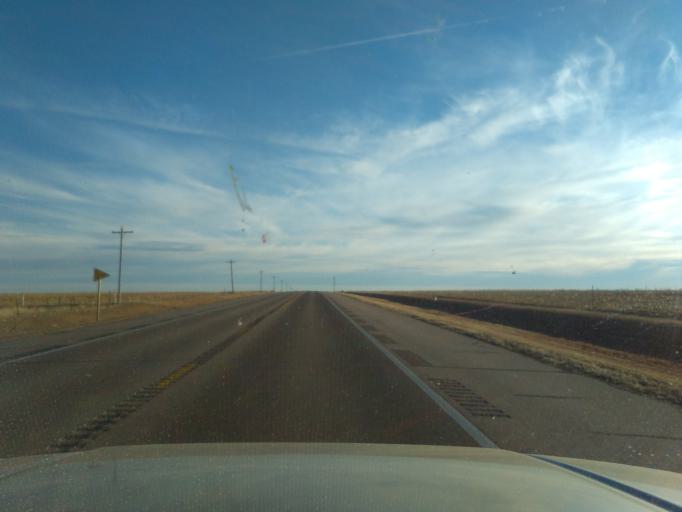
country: US
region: Kansas
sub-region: Logan County
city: Oakley
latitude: 39.1755
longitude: -100.8704
